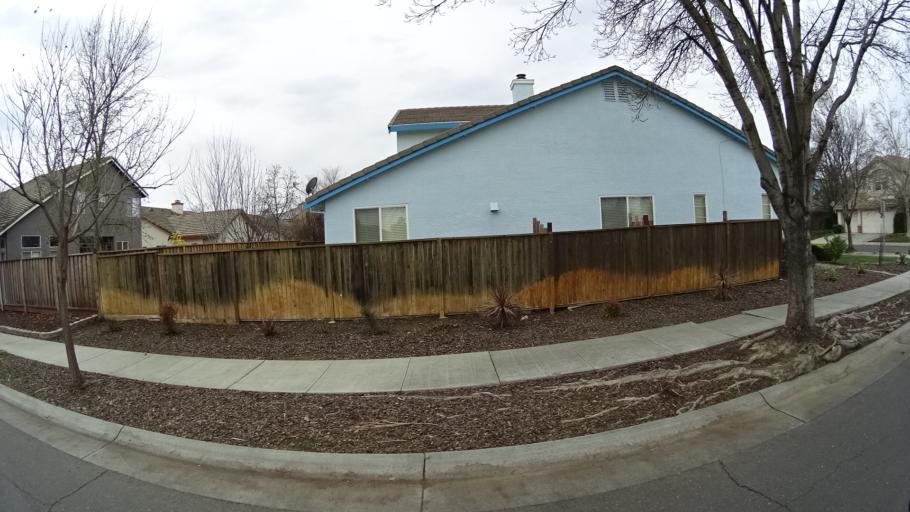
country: US
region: California
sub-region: Yolo County
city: Davis
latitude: 38.5573
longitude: -121.6991
